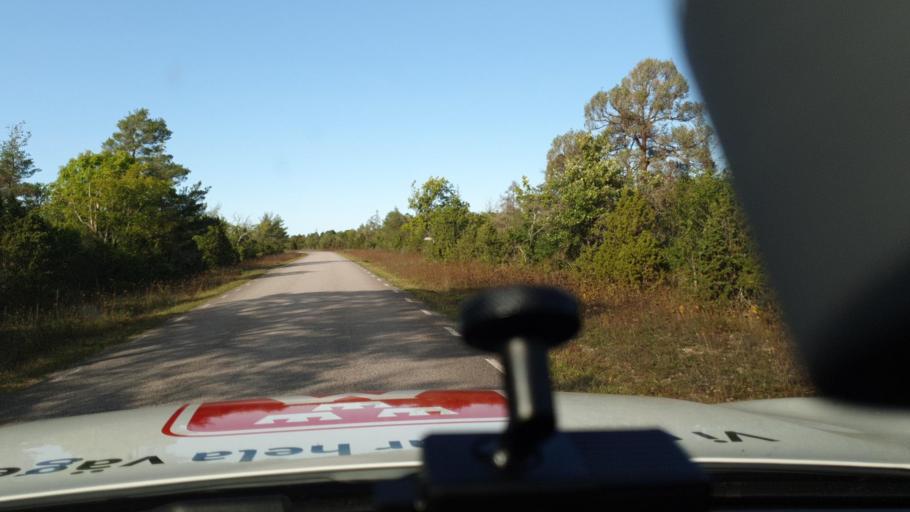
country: SE
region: Gotland
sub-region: Gotland
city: Slite
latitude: 57.6912
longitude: 18.6353
